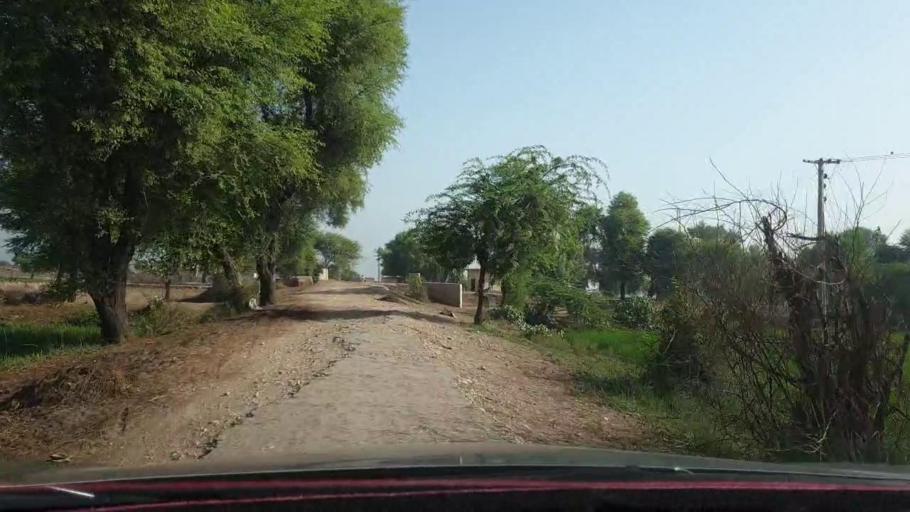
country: PK
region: Sindh
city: Nasirabad
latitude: 27.4486
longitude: 67.9194
